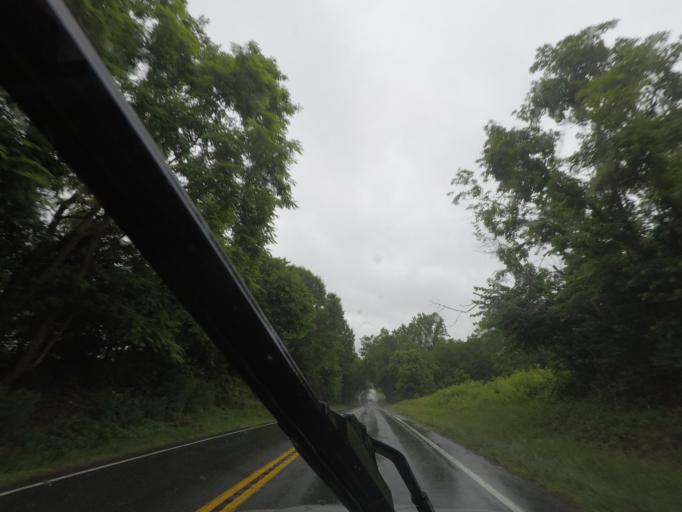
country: US
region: Virginia
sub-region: Orange County
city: Orange
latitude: 38.3387
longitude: -78.1242
